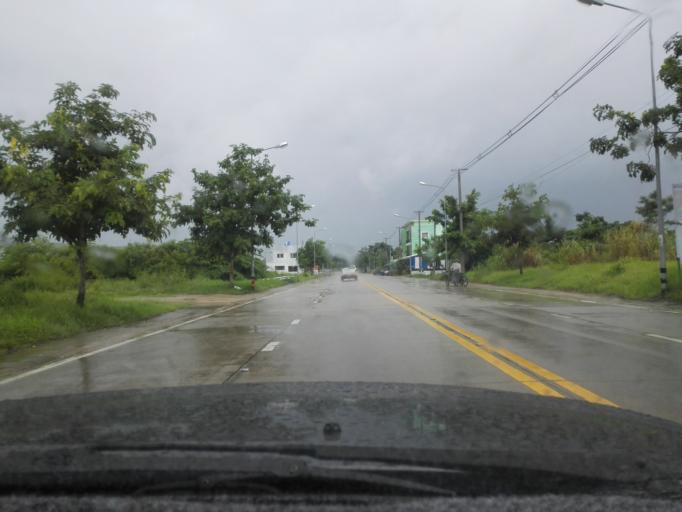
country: TH
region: Tak
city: Mae Sot
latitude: 16.7119
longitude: 98.5823
